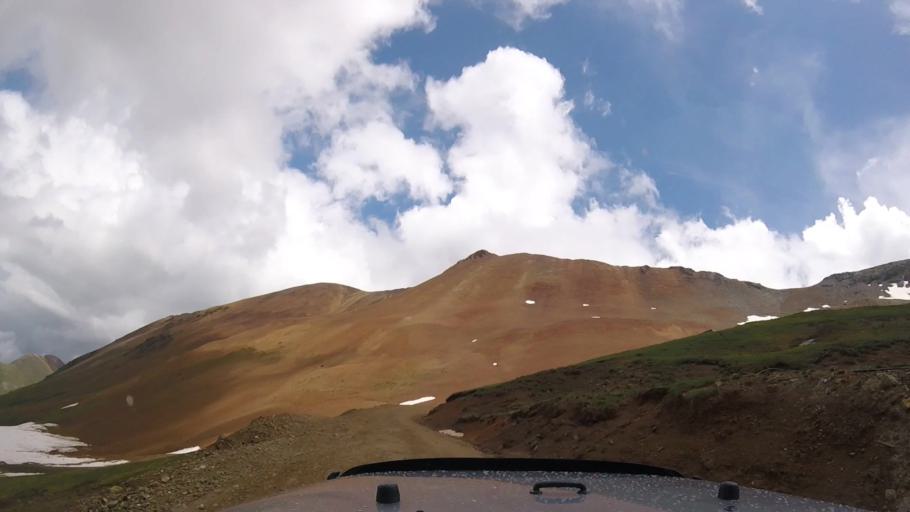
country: US
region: Colorado
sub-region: San Juan County
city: Silverton
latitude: 37.9165
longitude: -107.6126
